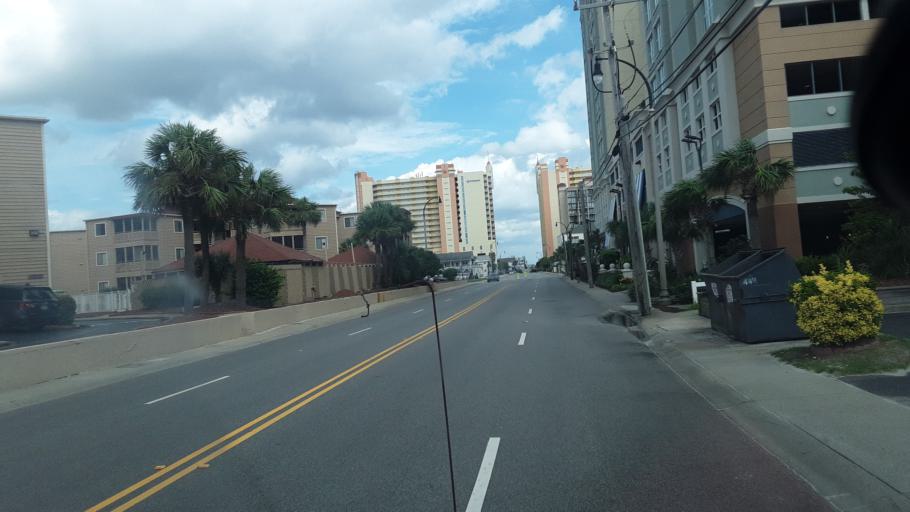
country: US
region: South Carolina
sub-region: Horry County
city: North Myrtle Beach
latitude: 33.8154
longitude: -78.6812
